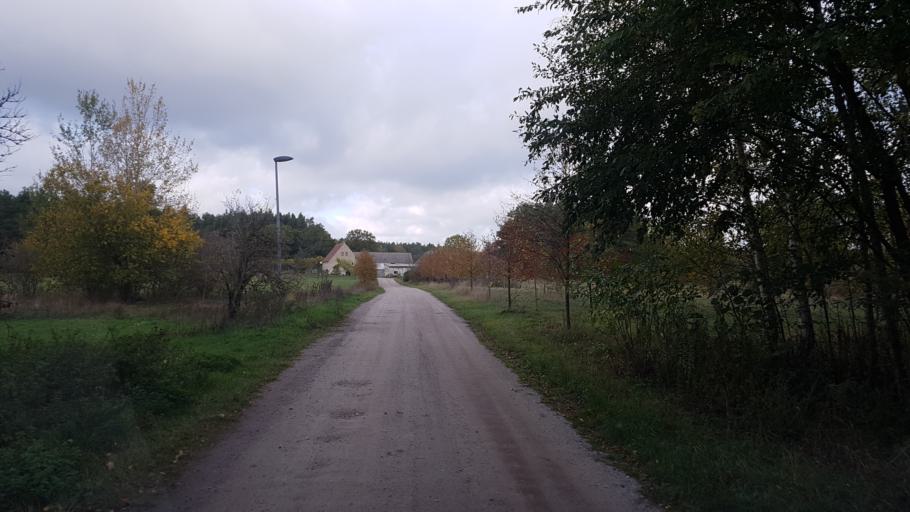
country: DE
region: Brandenburg
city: Schonborn
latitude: 51.6155
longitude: 13.5149
